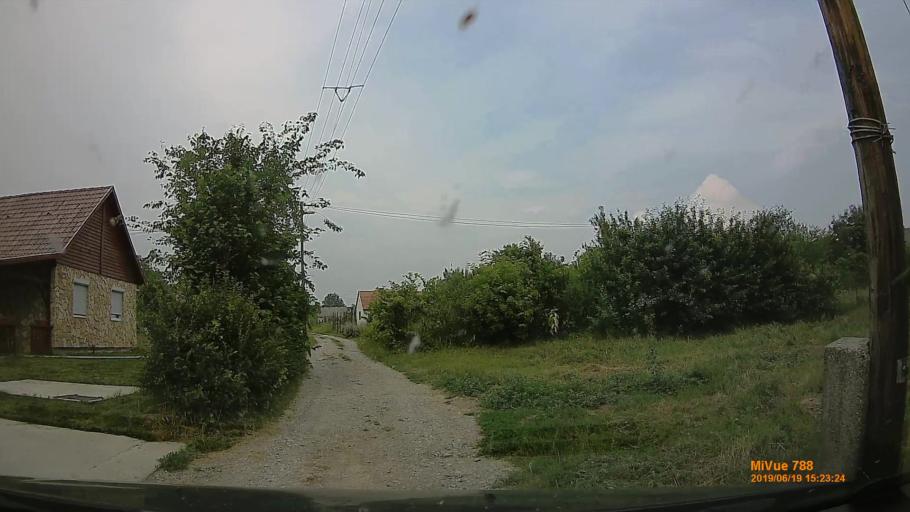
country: HU
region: Baranya
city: Szigetvar
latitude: 46.0746
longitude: 17.8470
